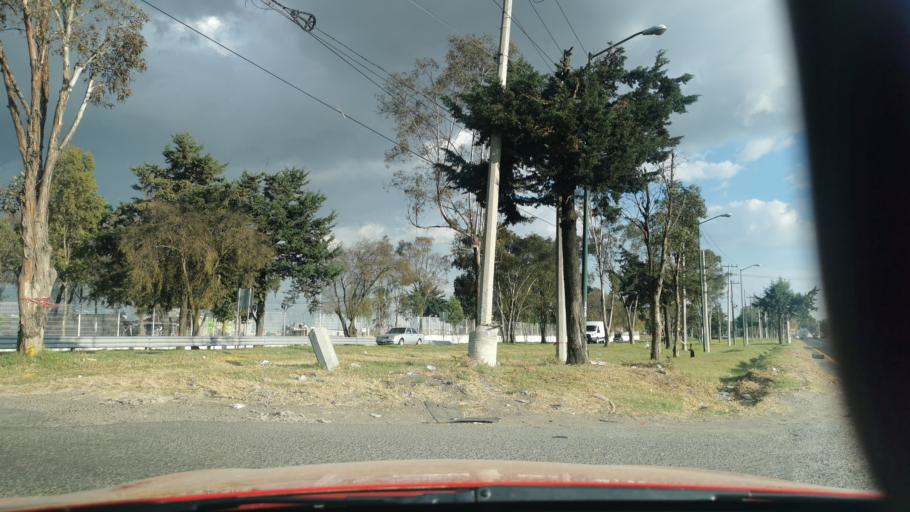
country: MX
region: Mexico
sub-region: Toluca
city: Barrio de Jesus Fraccion Primera
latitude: 19.3680
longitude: -99.6939
